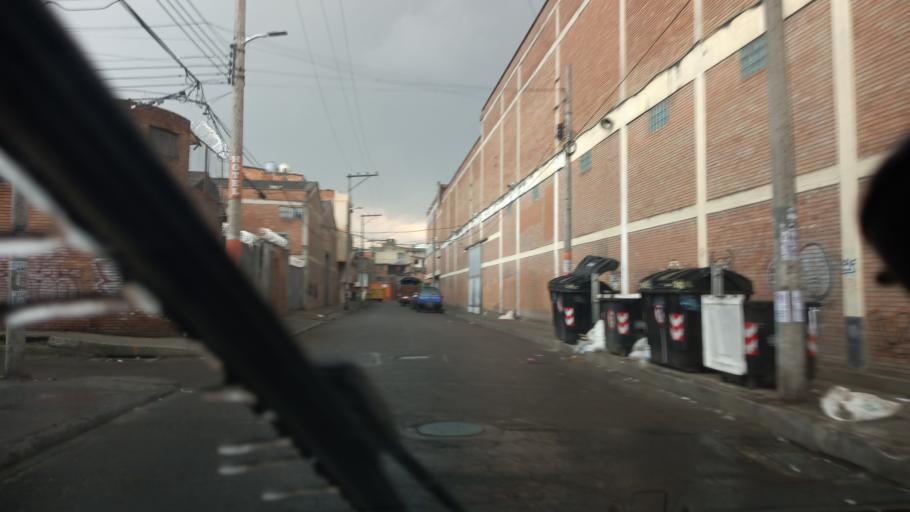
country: CO
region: Cundinamarca
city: Funza
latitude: 4.6707
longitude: -74.1424
